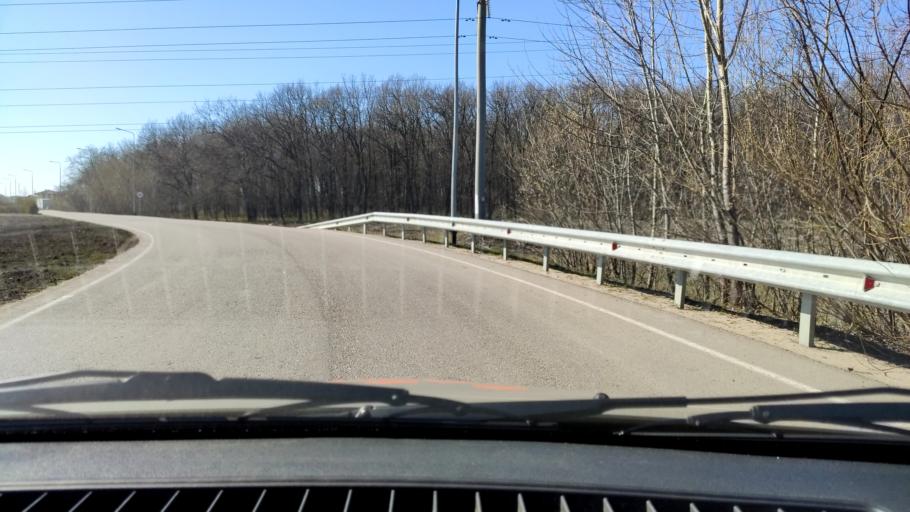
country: RU
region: Voronezj
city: Somovo
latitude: 51.6870
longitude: 39.3417
